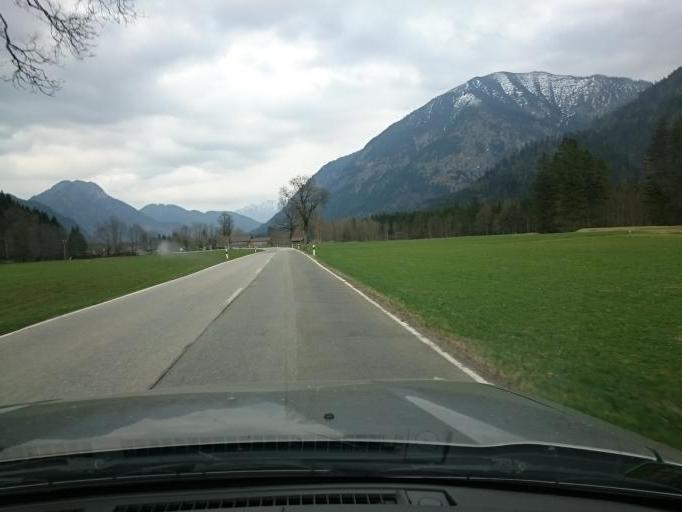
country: DE
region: Bavaria
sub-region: Upper Bavaria
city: Unterammergau
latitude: 47.5702
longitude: 11.0152
